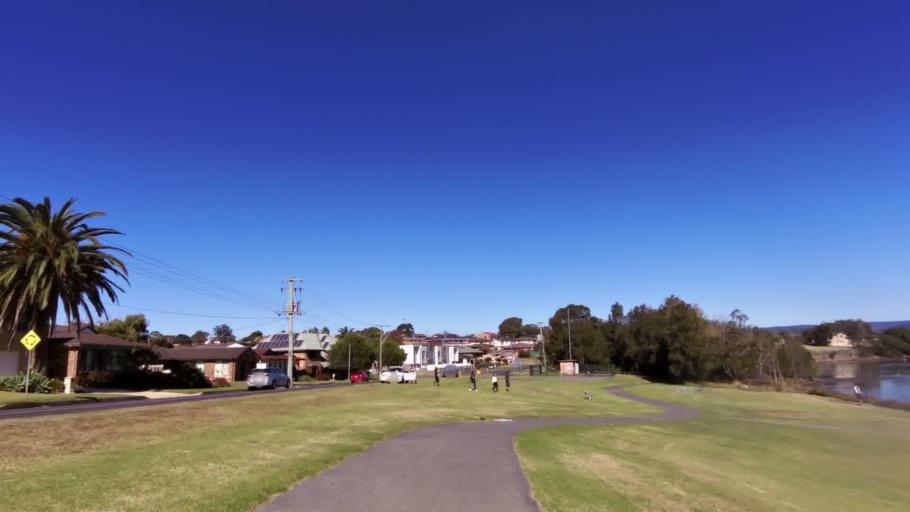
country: AU
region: New South Wales
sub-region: Shellharbour
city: Lake Illawarra
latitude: -34.5502
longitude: 150.8369
